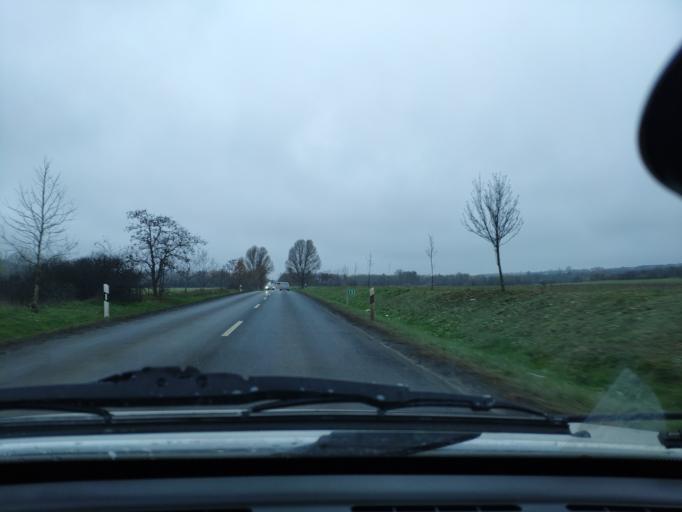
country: HU
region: Pest
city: Tarnok
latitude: 47.3950
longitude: 18.8454
